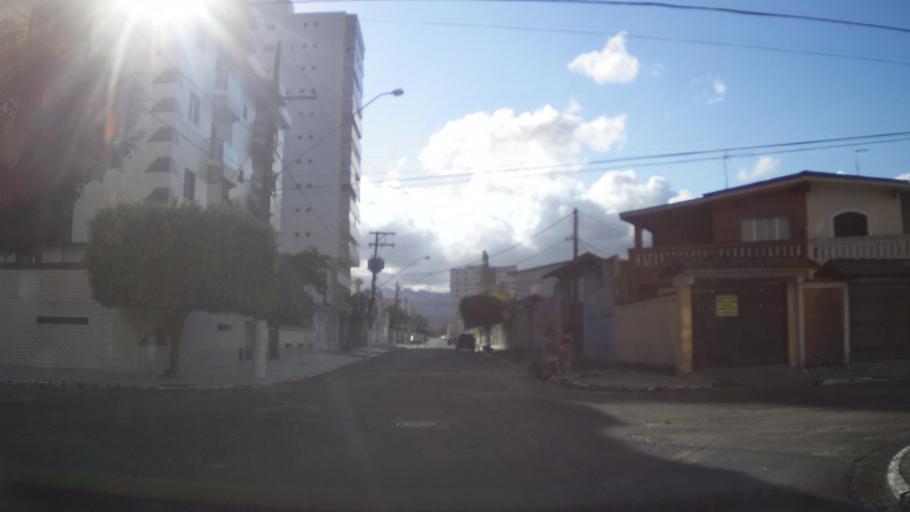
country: BR
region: Sao Paulo
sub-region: Praia Grande
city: Praia Grande
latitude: -24.0244
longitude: -46.4660
